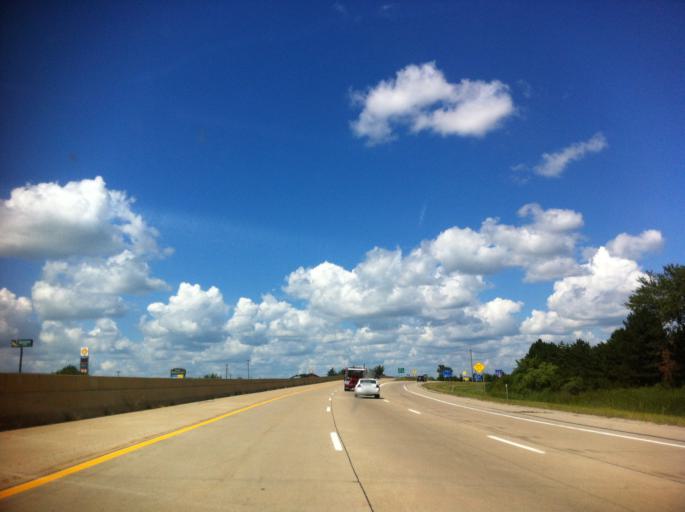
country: US
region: Michigan
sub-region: Monroe County
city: Dundee
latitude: 41.9554
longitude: -83.6717
